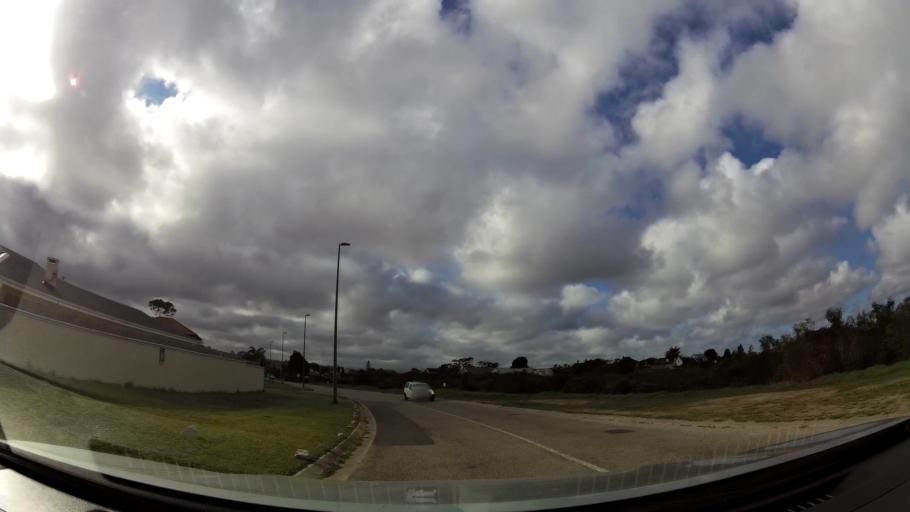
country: ZA
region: Western Cape
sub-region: Eden District Municipality
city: Plettenberg Bay
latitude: -34.0853
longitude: 23.3625
